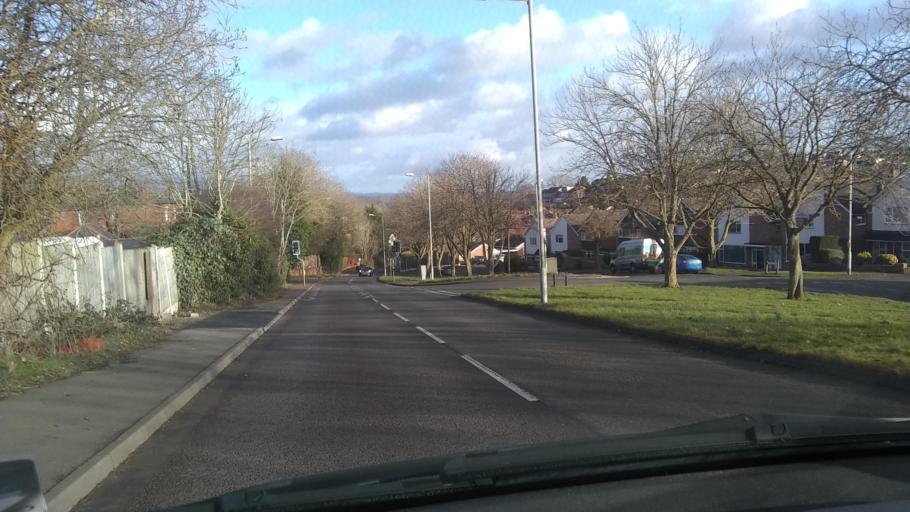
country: GB
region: England
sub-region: Worcestershire
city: Bewdley
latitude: 52.3753
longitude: -2.3296
